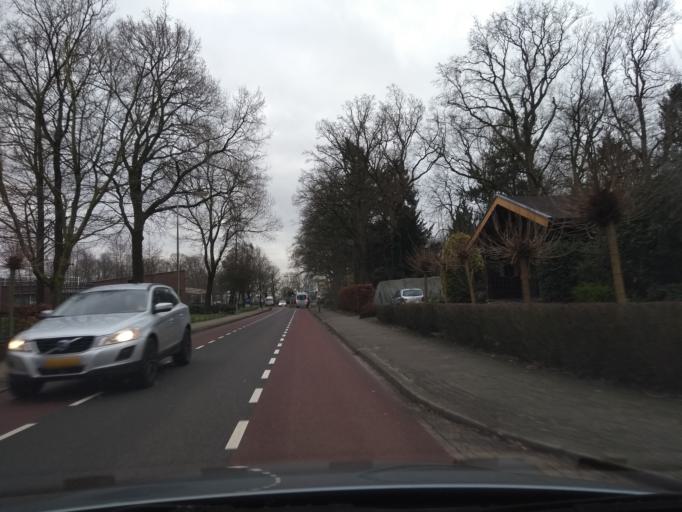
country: NL
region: Overijssel
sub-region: Gemeente Haaksbergen
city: Haaksbergen
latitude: 52.1600
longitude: 6.7512
